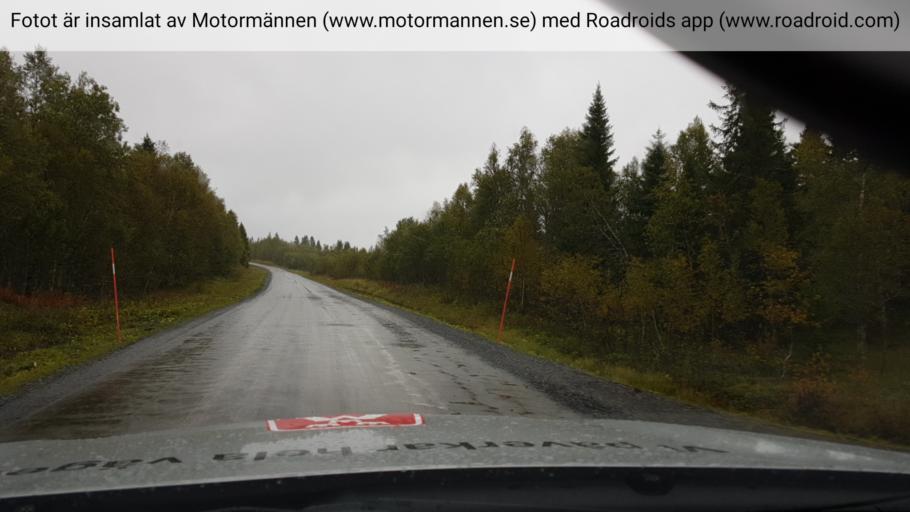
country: SE
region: Jaemtland
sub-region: Are Kommun
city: Are
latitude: 63.7057
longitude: 12.6524
